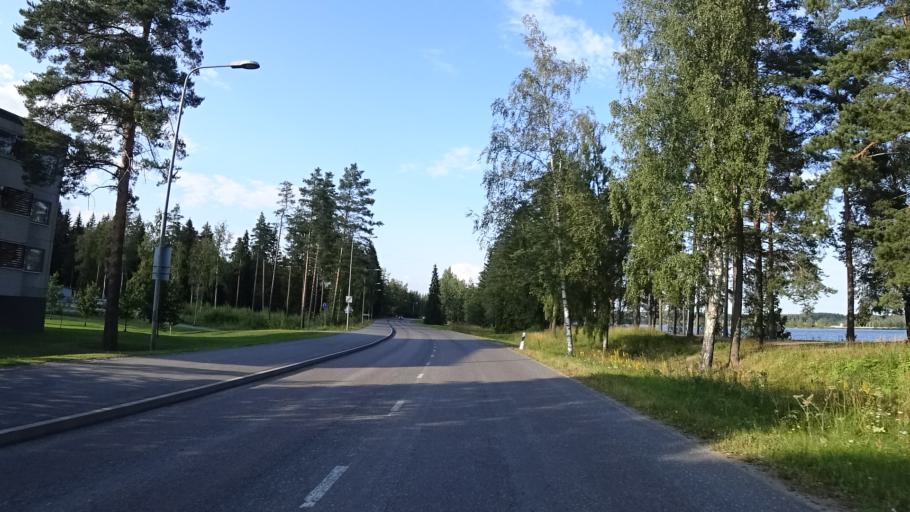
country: FI
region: South Karelia
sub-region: Imatra
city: Imatra
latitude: 61.1741
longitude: 28.7772
